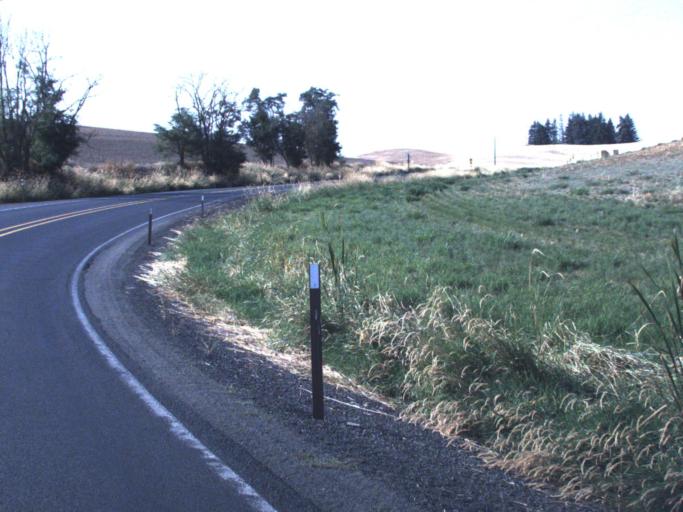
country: US
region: Idaho
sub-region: Benewah County
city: Plummer
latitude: 47.1991
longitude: -117.0935
